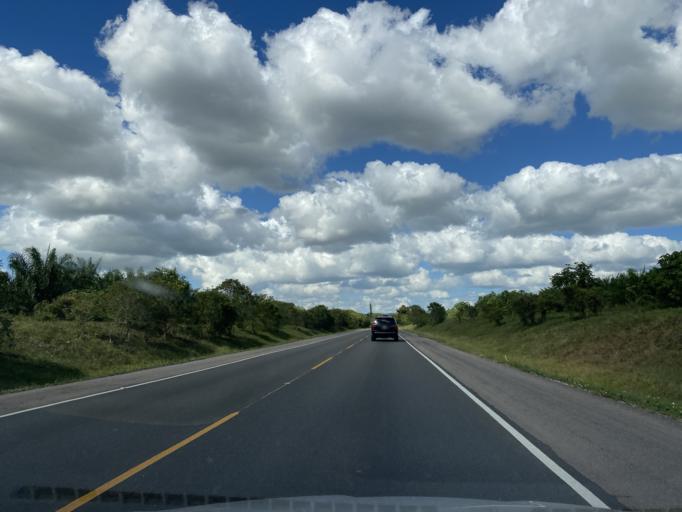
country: DO
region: Monte Plata
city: Monte Plata
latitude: 18.7383
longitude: -69.7632
